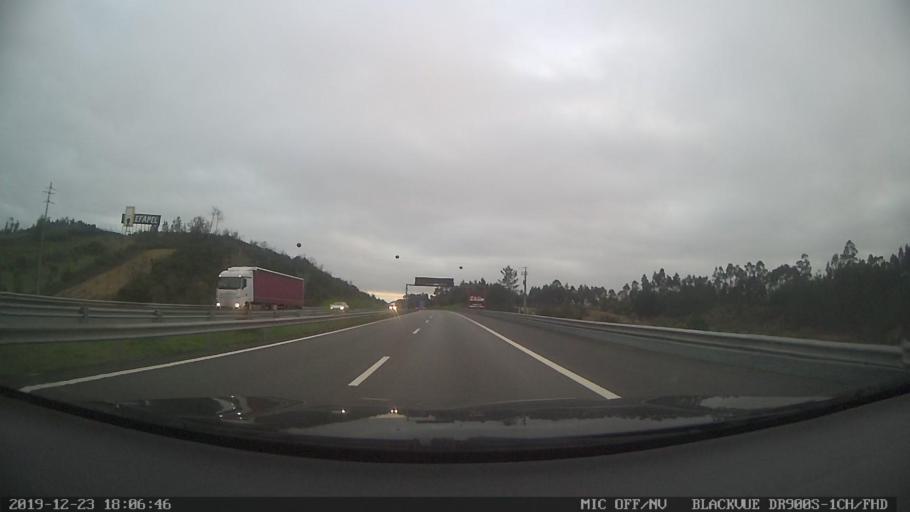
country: PT
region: Aveiro
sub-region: Mealhada
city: Pampilhosa do Botao
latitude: 40.2984
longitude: -8.4861
